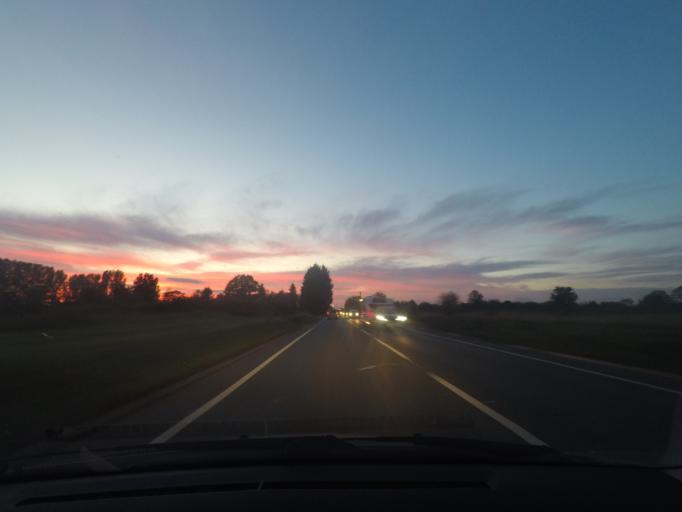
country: GB
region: England
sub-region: East Riding of Yorkshire
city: Thornton
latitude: 53.9311
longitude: -0.8289
